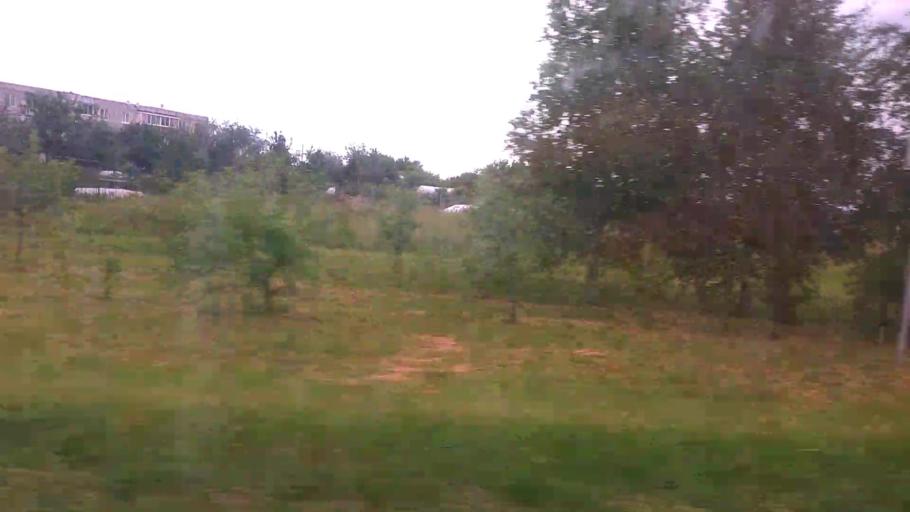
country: RU
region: Moskovskaya
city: Ozery
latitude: 54.7710
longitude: 38.6451
